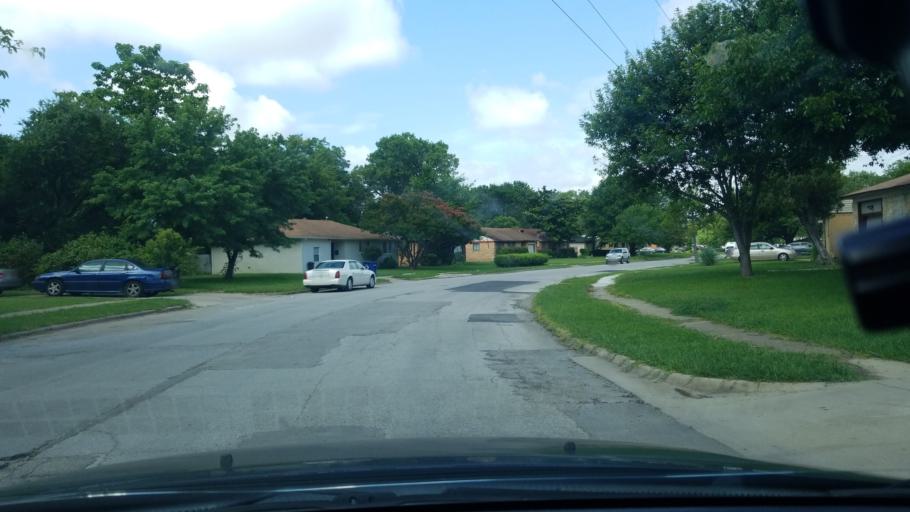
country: US
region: Texas
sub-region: Dallas County
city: Mesquite
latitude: 32.8183
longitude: -96.6501
